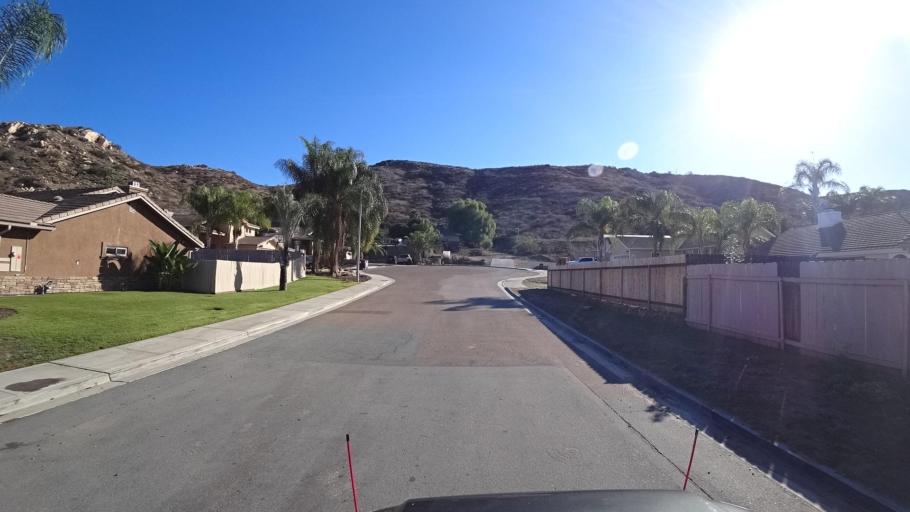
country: US
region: California
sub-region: San Diego County
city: Lakeside
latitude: 32.8467
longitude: -116.9147
